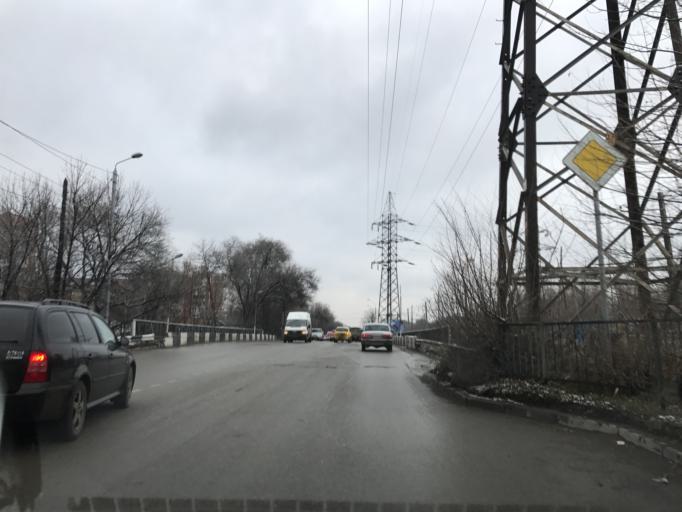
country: RU
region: Rostov
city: Rostov-na-Donu
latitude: 47.2447
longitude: 39.7122
